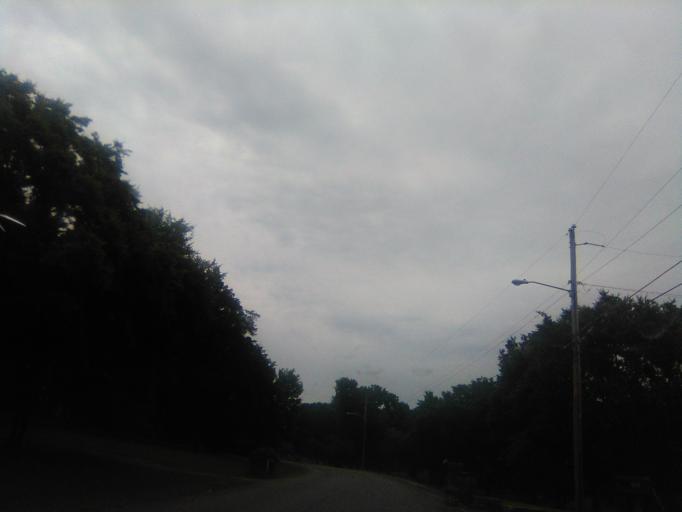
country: US
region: Tennessee
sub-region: Davidson County
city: Belle Meade
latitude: 36.1169
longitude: -86.8934
